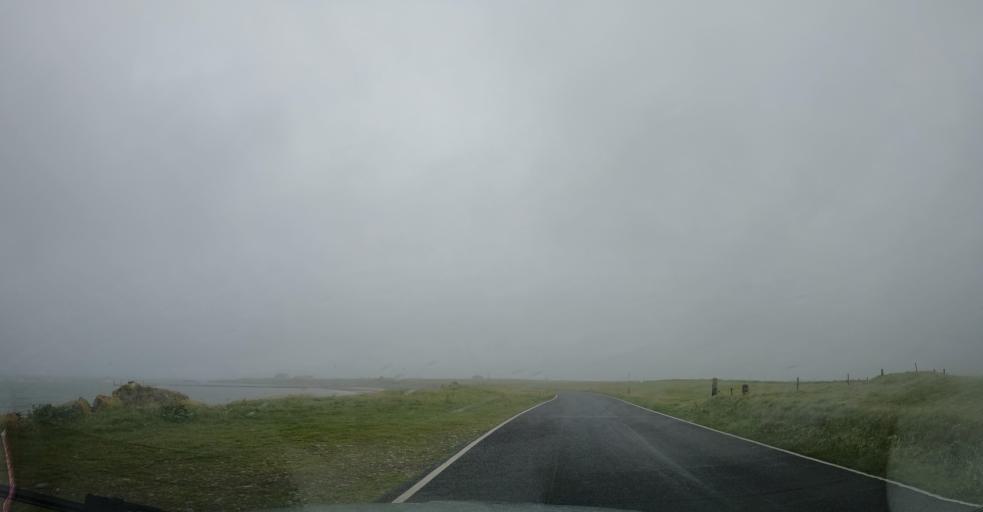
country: GB
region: Scotland
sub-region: Eilean Siar
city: Benbecula
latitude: 57.4457
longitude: -7.3998
